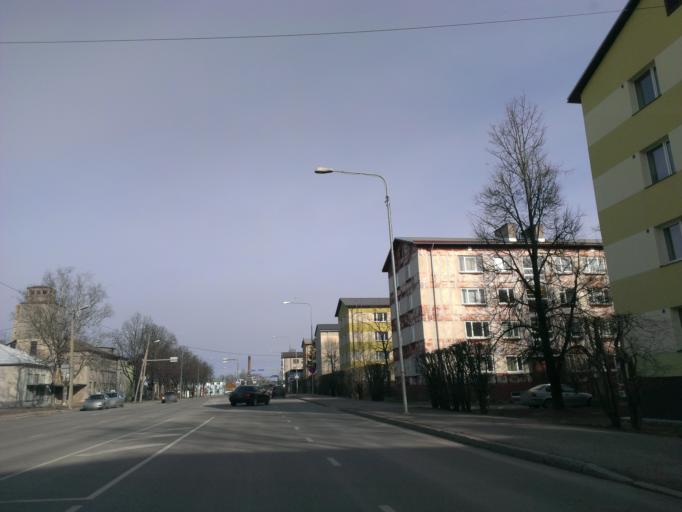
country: EE
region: Paernumaa
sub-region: Paernu linn
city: Parnu
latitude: 58.3912
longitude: 24.4911
